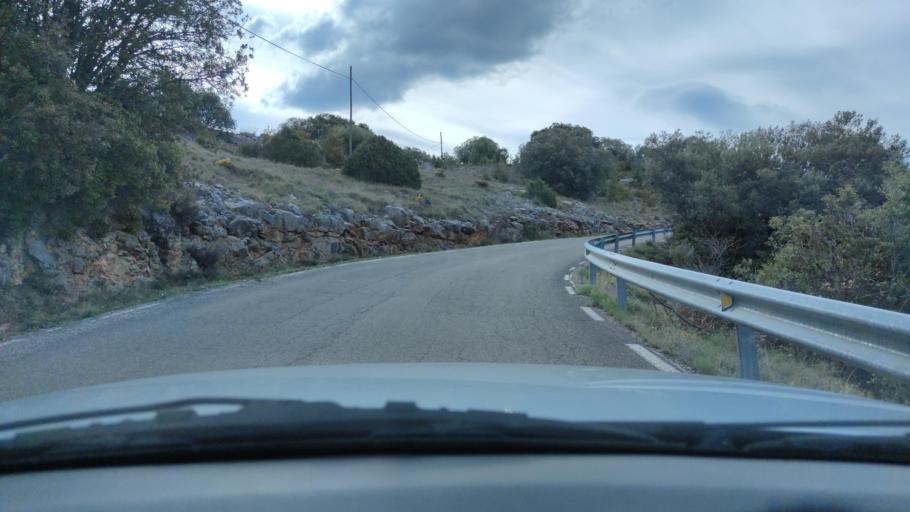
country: ES
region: Catalonia
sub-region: Provincia de Lleida
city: Coll de Nargo
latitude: 42.2400
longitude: 1.3722
